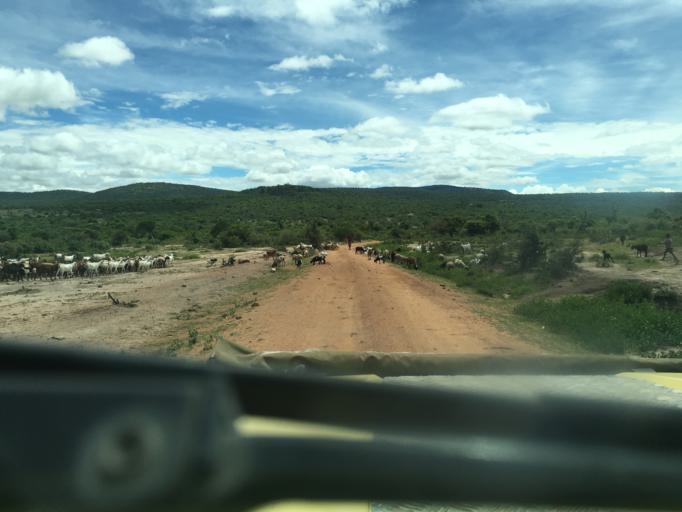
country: TZ
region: Mara
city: Mugumu
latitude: -1.8890
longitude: 35.3748
